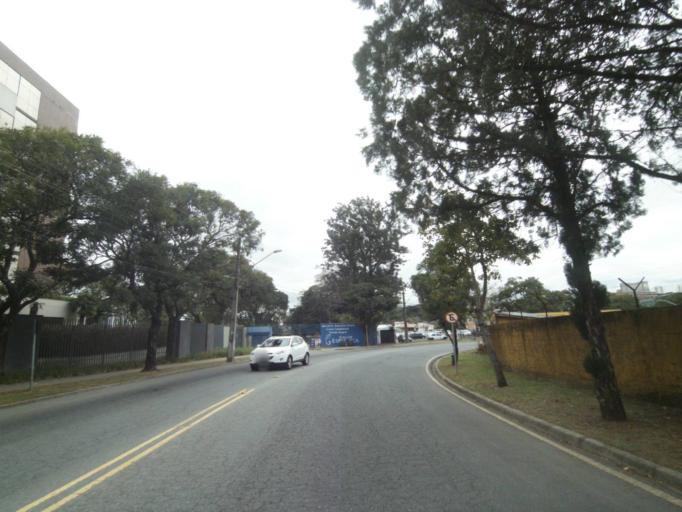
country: BR
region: Parana
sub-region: Curitiba
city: Curitiba
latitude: -25.4518
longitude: -49.2458
